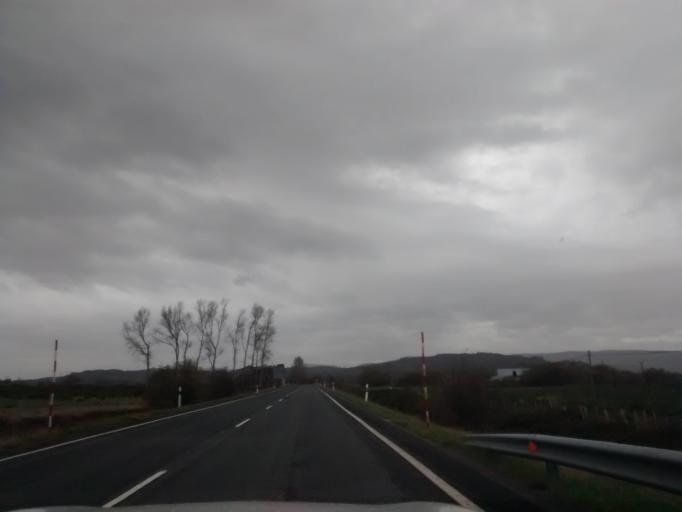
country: ES
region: Castille and Leon
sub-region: Provincia de Burgos
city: Arija
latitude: 43.0179
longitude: -3.8548
